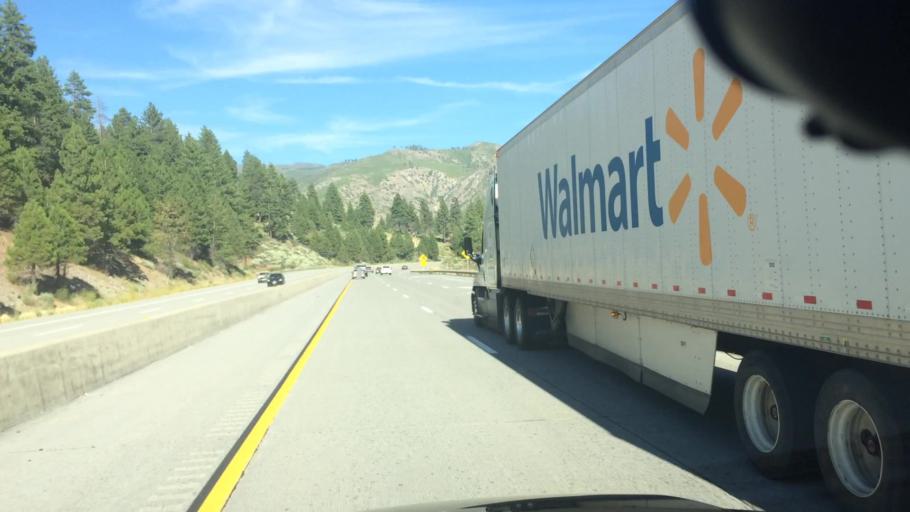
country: US
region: California
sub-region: Placer County
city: Tahoe Vista
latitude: 39.3724
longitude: -120.0562
